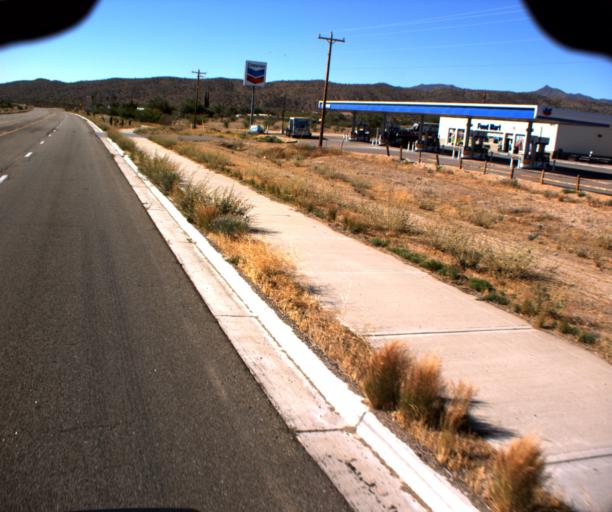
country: US
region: Arizona
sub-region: Yavapai County
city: Bagdad
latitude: 34.7048
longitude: -113.6118
